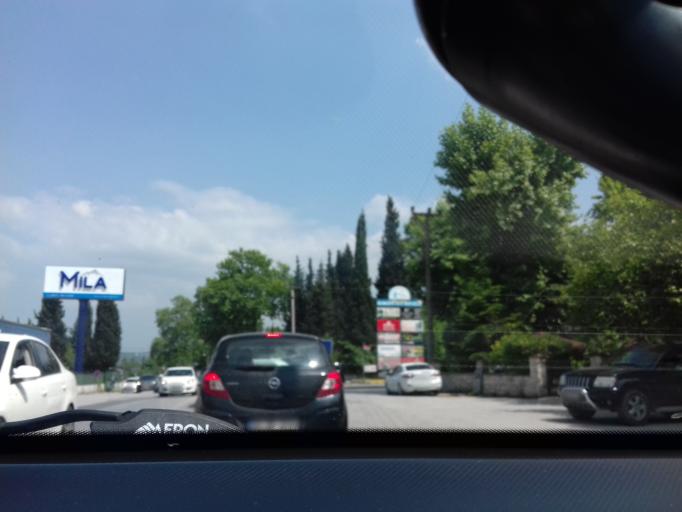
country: TR
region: Sakarya
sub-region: Merkez
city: Sapanca
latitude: 40.6887
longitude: 30.2356
